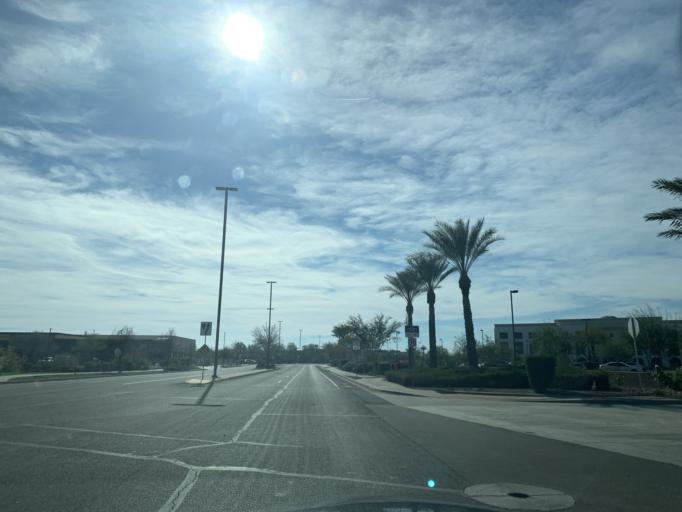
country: US
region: Arizona
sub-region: Maricopa County
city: Gilbert
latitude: 33.2888
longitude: -111.7488
